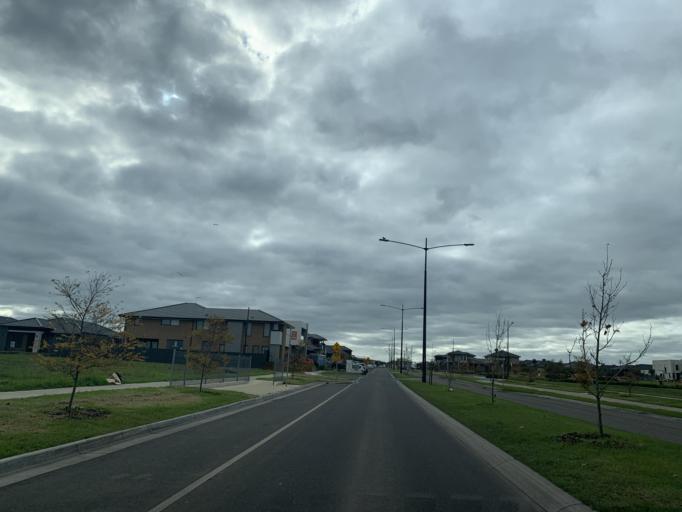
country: AU
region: Victoria
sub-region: Whittlesea
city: Epping
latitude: -37.6049
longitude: 145.0060
